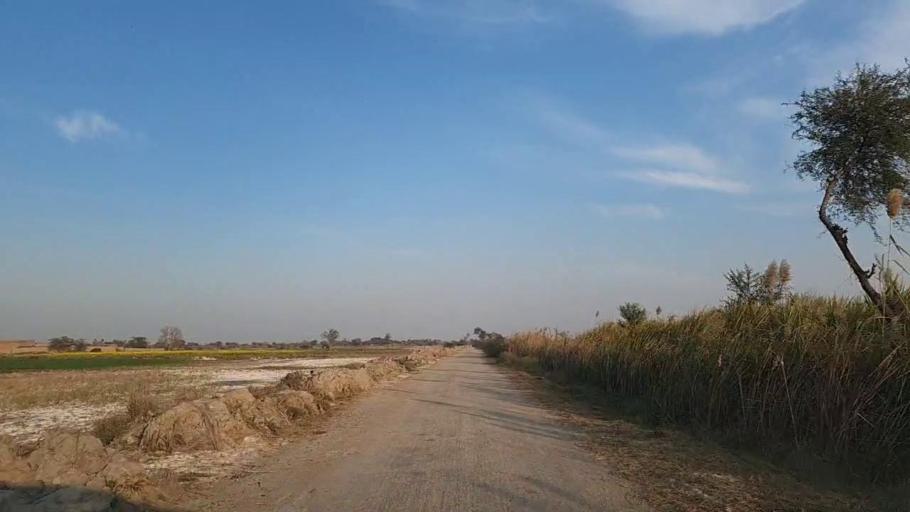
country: PK
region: Sindh
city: Bandhi
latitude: 26.5743
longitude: 68.3444
